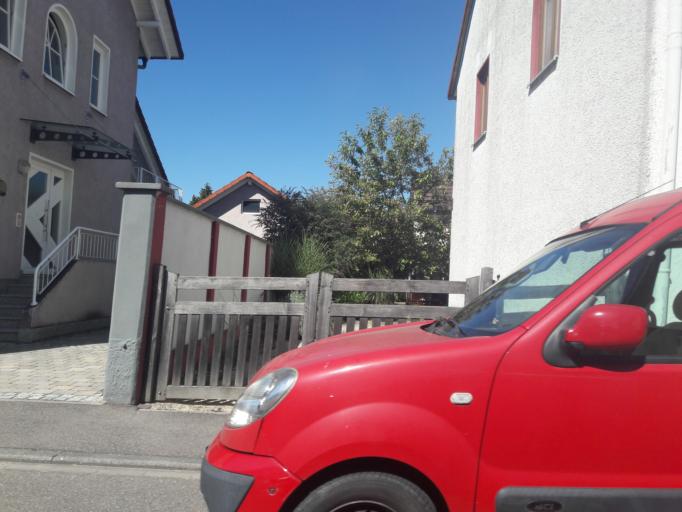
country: DE
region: Baden-Wuerttemberg
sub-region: Karlsruhe Region
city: Ubstadt-Weiher
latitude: 49.1404
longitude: 8.6643
